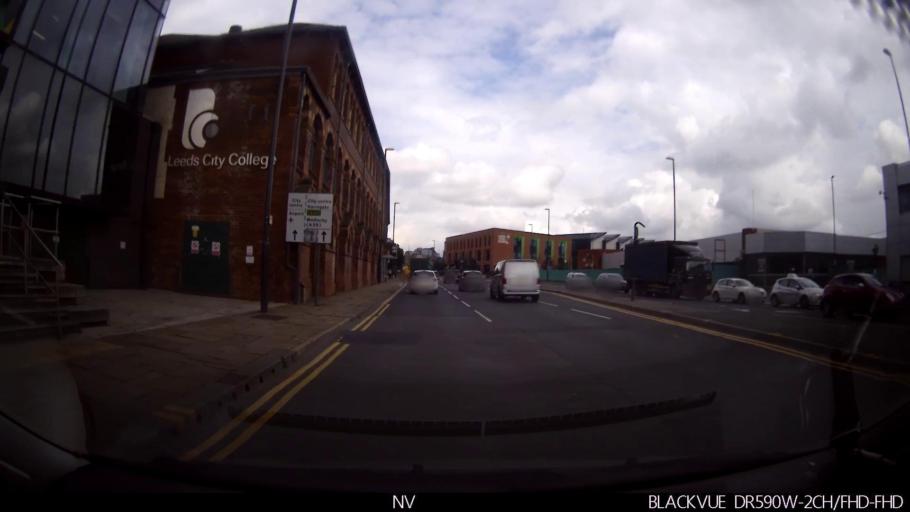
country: GB
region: England
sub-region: City and Borough of Leeds
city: Leeds
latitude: 53.7886
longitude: -1.5360
